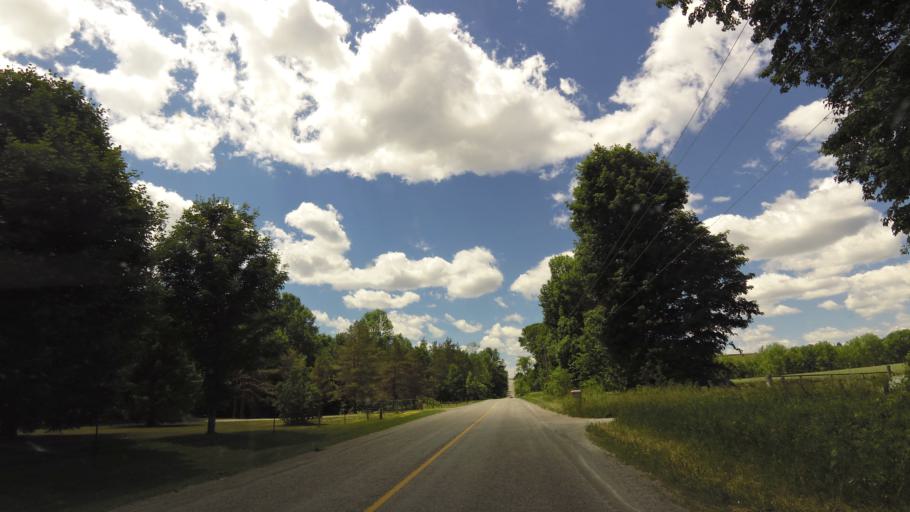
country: CA
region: Ontario
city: Oshawa
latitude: 43.9653
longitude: -78.5493
